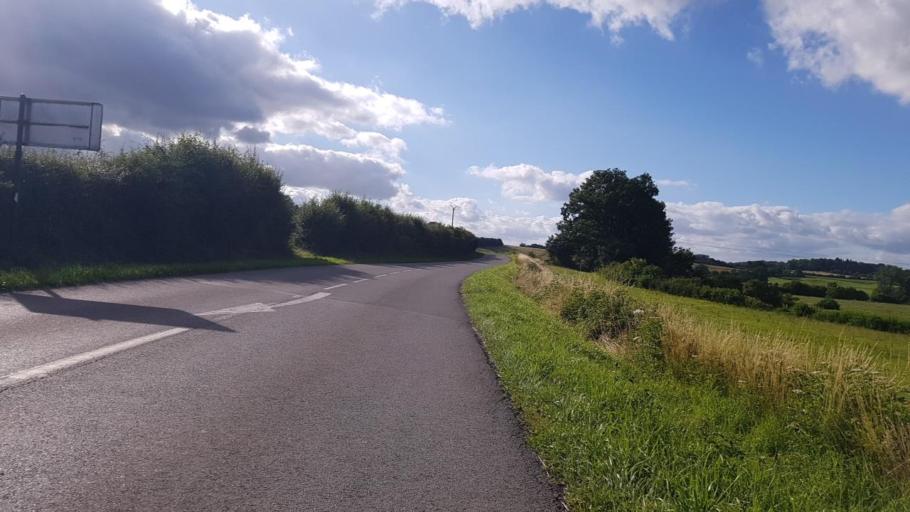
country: FR
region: Picardie
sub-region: Departement de l'Aisne
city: Hirson
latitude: 49.9211
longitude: 4.0556
